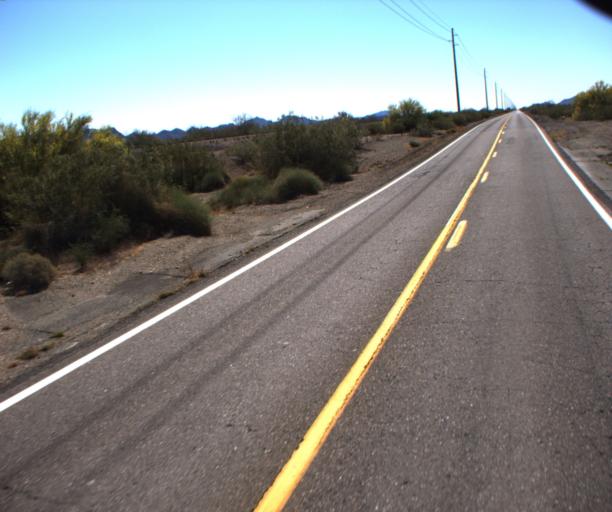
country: US
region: Arizona
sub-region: La Paz County
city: Salome
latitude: 33.7976
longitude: -113.8303
